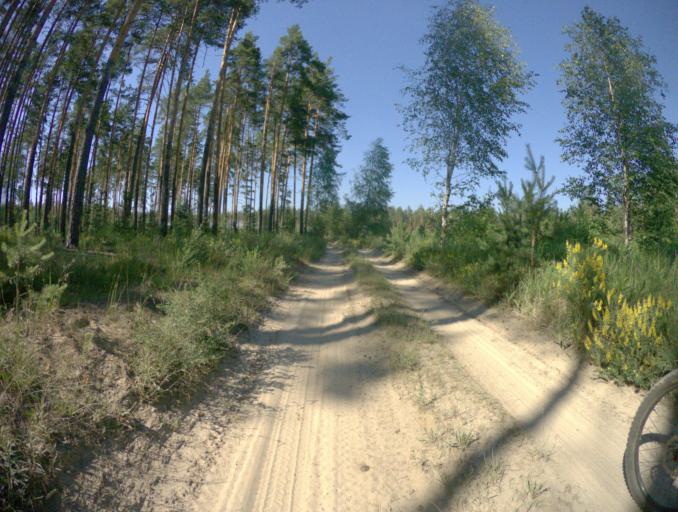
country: RU
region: Vladimir
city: Vyazniki
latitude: 56.3702
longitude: 42.1907
